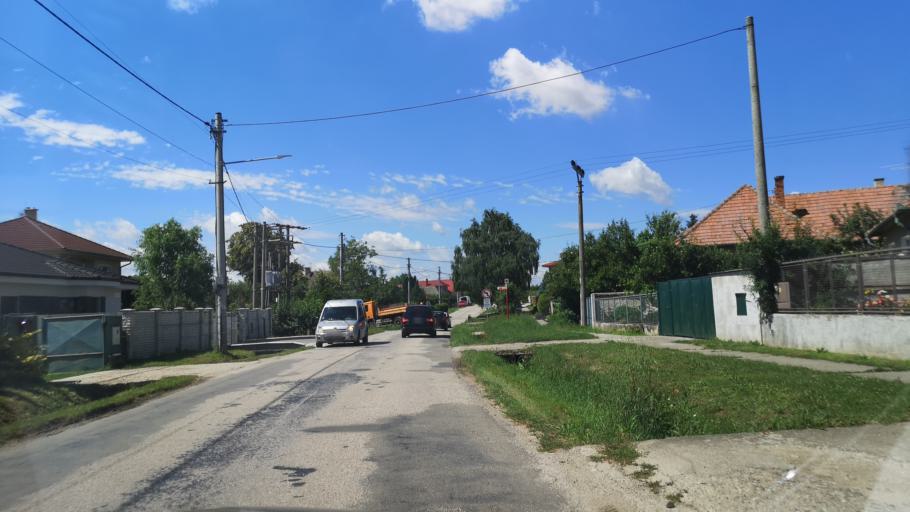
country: SK
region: Nitriansky
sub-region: Okres Nitra
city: Nitra
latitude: 48.2813
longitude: 17.9710
